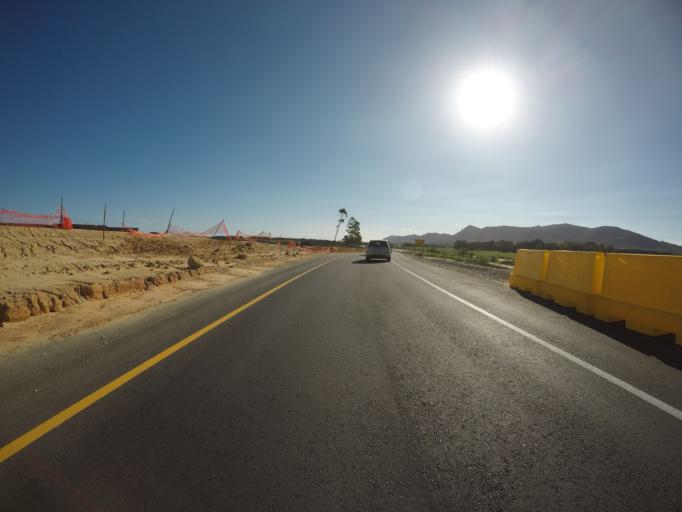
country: ZA
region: Eastern Cape
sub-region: Nelson Mandela Bay Metropolitan Municipality
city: Uitenhage
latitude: -33.9196
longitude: 25.2934
